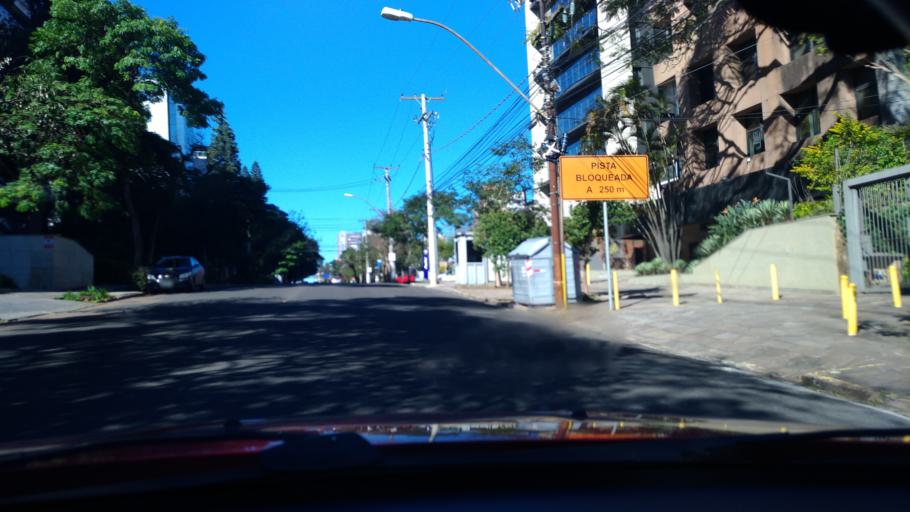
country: BR
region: Rio Grande do Sul
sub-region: Porto Alegre
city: Porto Alegre
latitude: -30.0177
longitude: -51.1915
